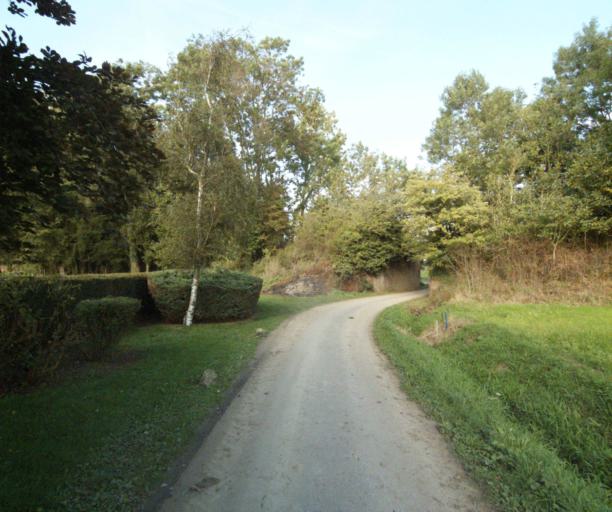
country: FR
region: Nord-Pas-de-Calais
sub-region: Departement du Nord
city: Radinghem-en-Weppes
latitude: 50.6353
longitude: 2.9188
